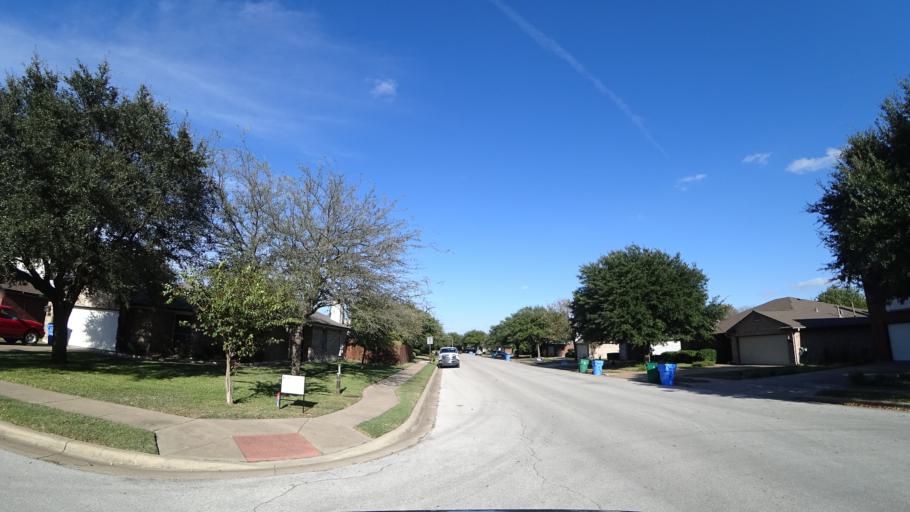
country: US
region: Texas
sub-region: Travis County
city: Wells Branch
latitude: 30.4624
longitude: -97.6864
